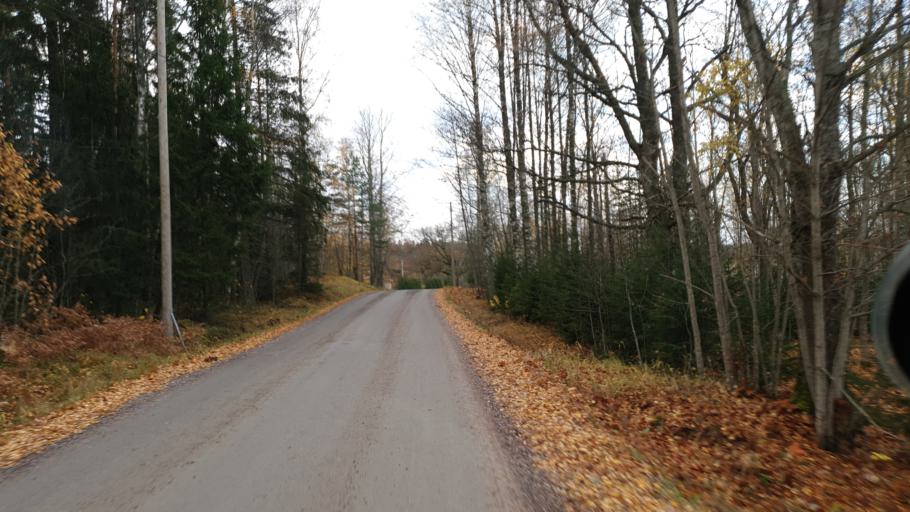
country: FI
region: Uusimaa
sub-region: Helsinki
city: Siuntio
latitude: 60.1283
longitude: 24.2802
